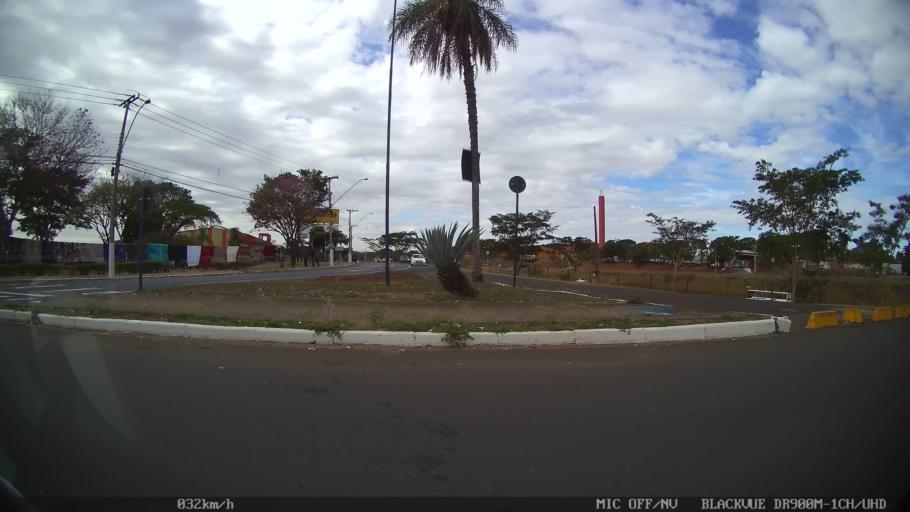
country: BR
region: Sao Paulo
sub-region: Bady Bassitt
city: Bady Bassitt
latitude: -20.8078
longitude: -49.5066
